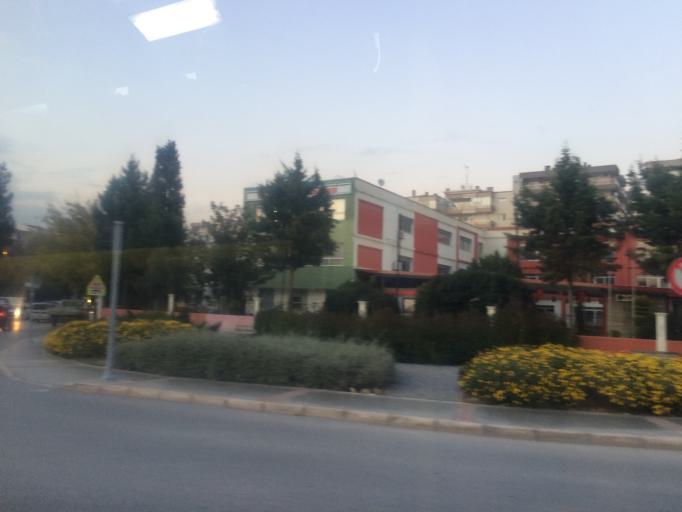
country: TR
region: Izmir
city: Karsiyaka
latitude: 38.4646
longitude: 27.0957
